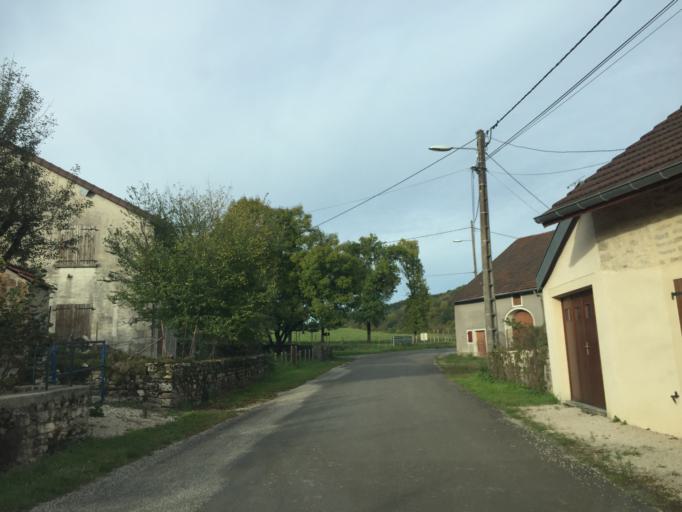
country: FR
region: Franche-Comte
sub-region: Departement du Jura
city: Orgelet
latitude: 46.5260
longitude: 5.5322
